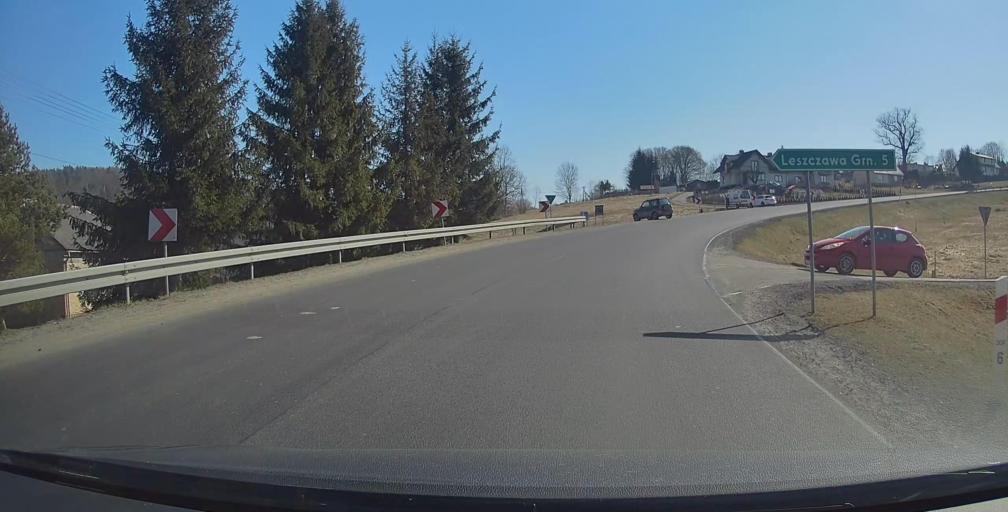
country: PL
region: Subcarpathian Voivodeship
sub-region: Powiat przemyski
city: Bircza
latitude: 49.6621
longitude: 22.4336
